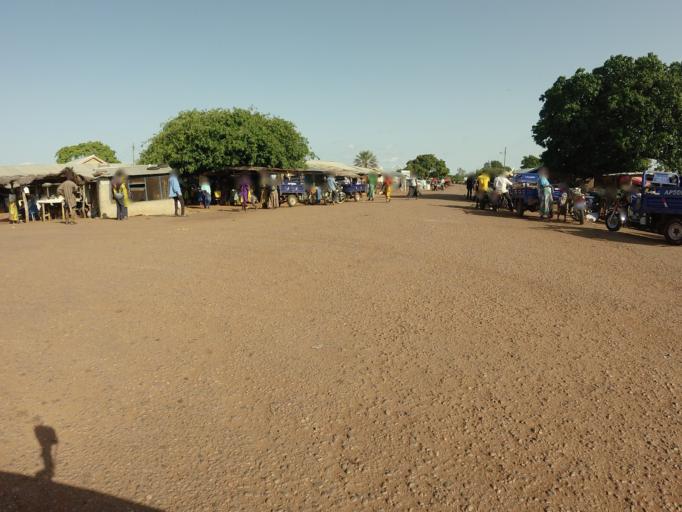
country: GH
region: Upper East
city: Bawku
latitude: 10.6326
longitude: -0.1805
